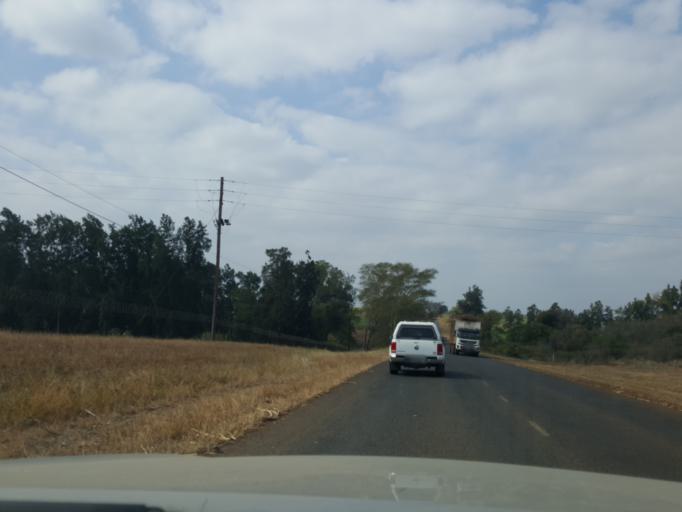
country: ZA
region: Mpumalanga
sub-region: Ehlanzeni District
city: Komatipoort
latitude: -25.3886
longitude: 31.8895
